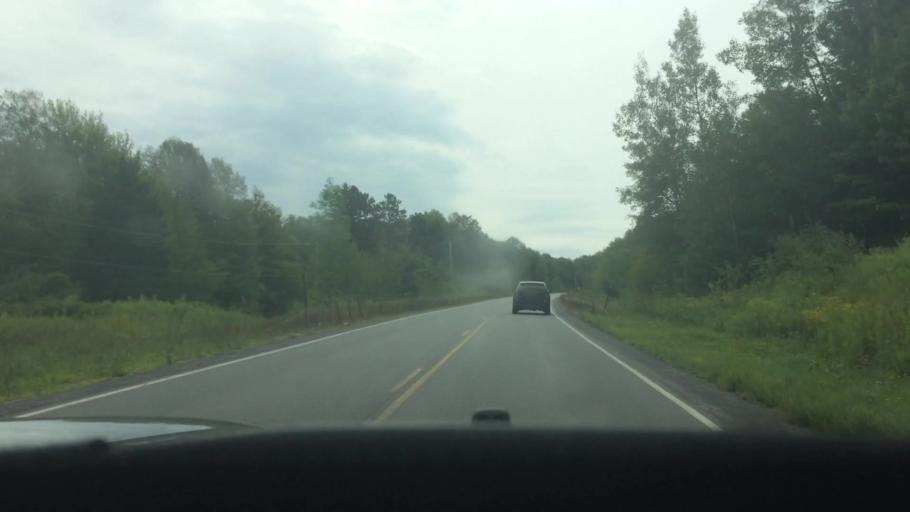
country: US
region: New York
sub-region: St. Lawrence County
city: Canton
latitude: 44.4813
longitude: -75.2446
